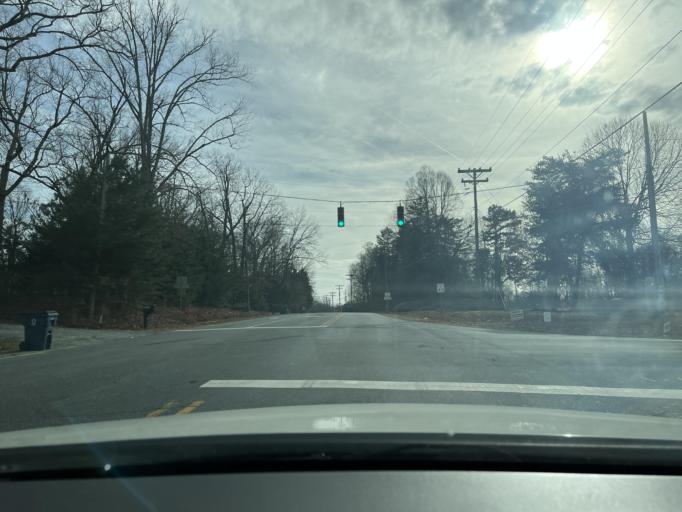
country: US
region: North Carolina
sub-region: Guilford County
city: Pleasant Garden
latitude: 36.0165
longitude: -79.7763
